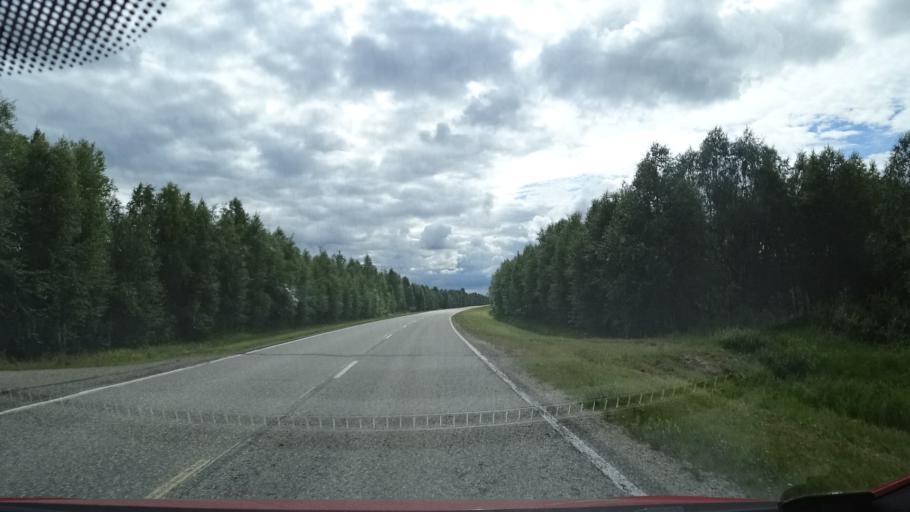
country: FI
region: Lapland
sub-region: Tunturi-Lappi
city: Kittilae
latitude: 67.4654
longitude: 24.9492
